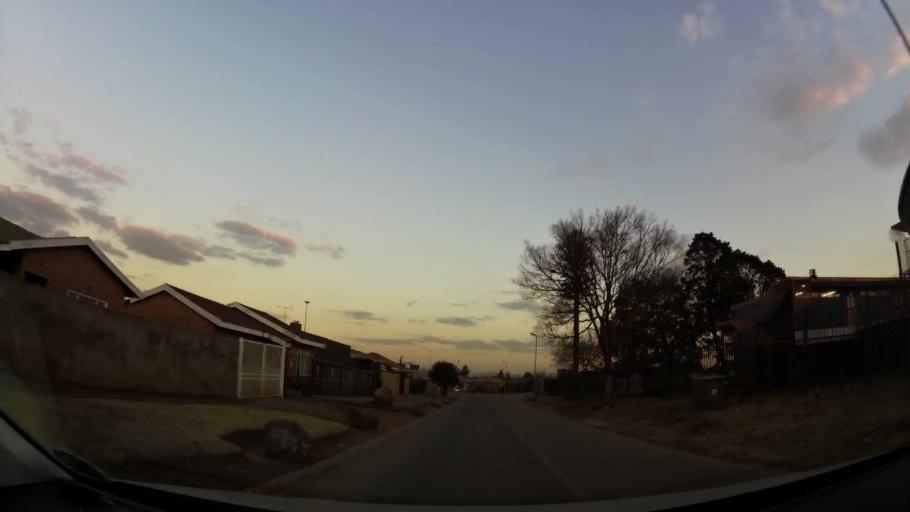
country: ZA
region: Gauteng
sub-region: City of Johannesburg Metropolitan Municipality
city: Soweto
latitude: -26.2741
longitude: 27.9043
